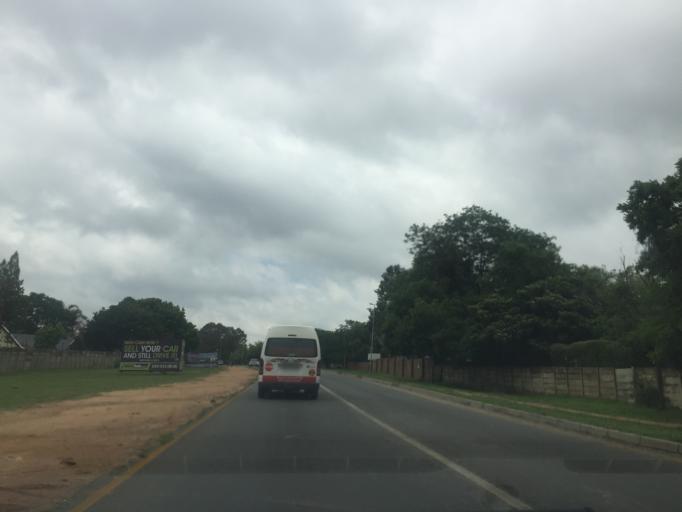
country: ZA
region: Gauteng
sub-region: City of Johannesburg Metropolitan Municipality
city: Johannesburg
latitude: -26.1019
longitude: 27.9870
